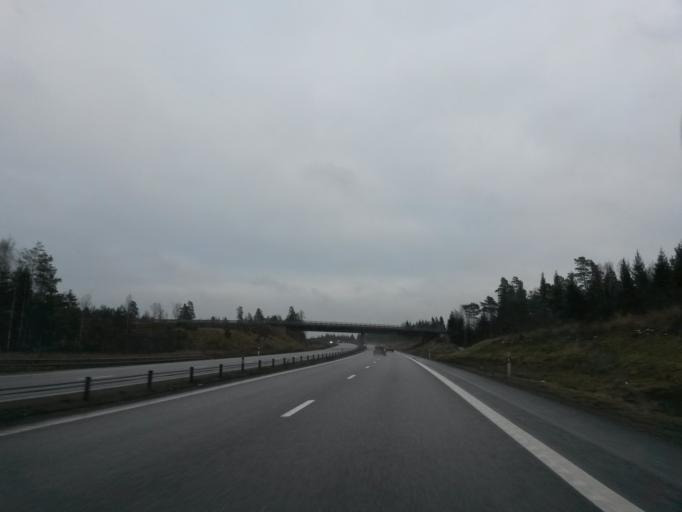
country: SE
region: Vaestra Goetaland
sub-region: Trollhattan
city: Sjuntorp
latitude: 58.3262
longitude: 12.1535
